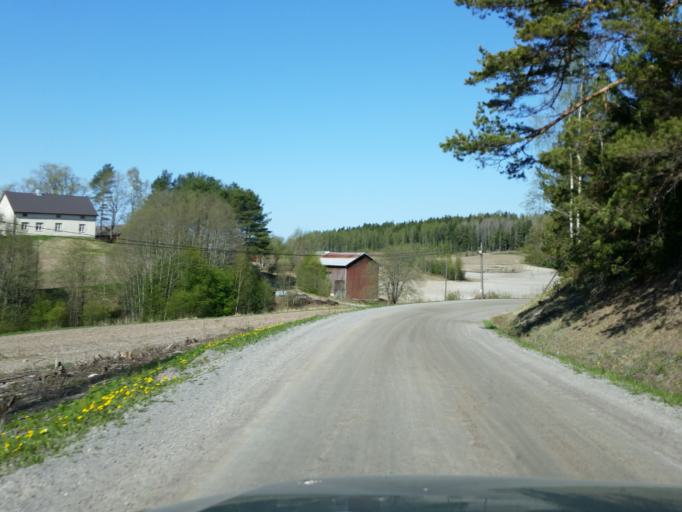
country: FI
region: Uusimaa
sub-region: Raaseporin
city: Karis
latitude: 60.1550
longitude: 23.6665
